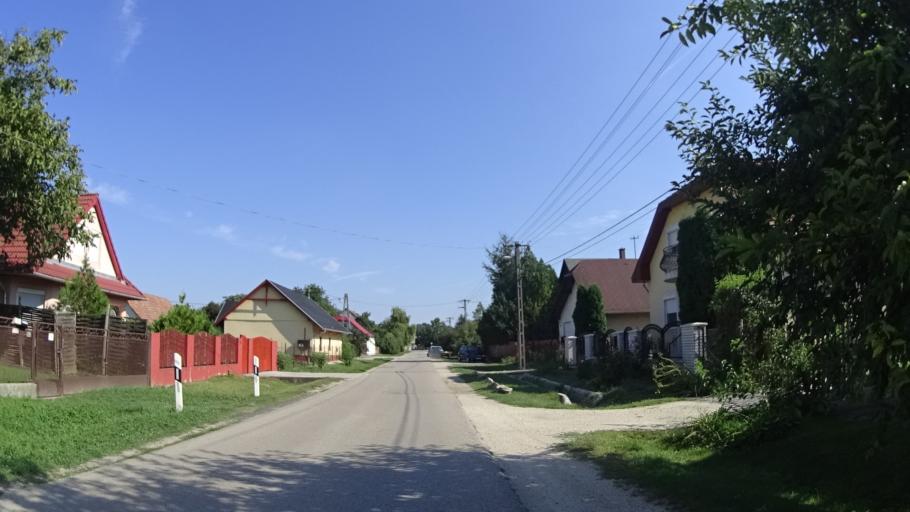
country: HU
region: Fejer
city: Kapolnasnyek
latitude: 47.2423
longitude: 18.6768
